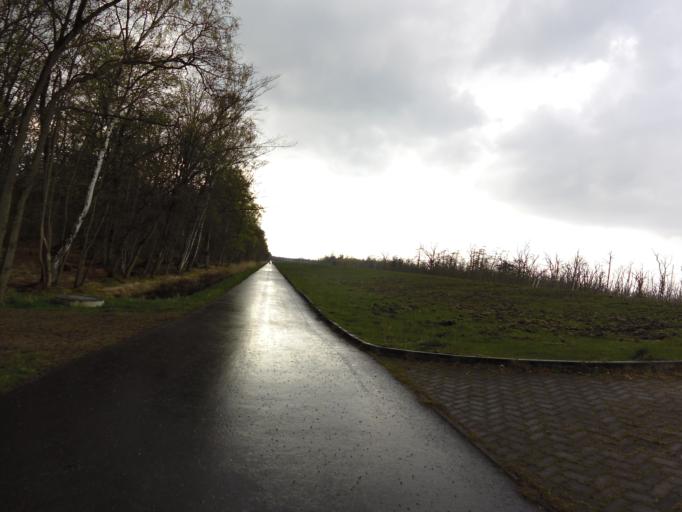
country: DE
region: Mecklenburg-Vorpommern
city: Barth
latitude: 54.4334
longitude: 12.8007
